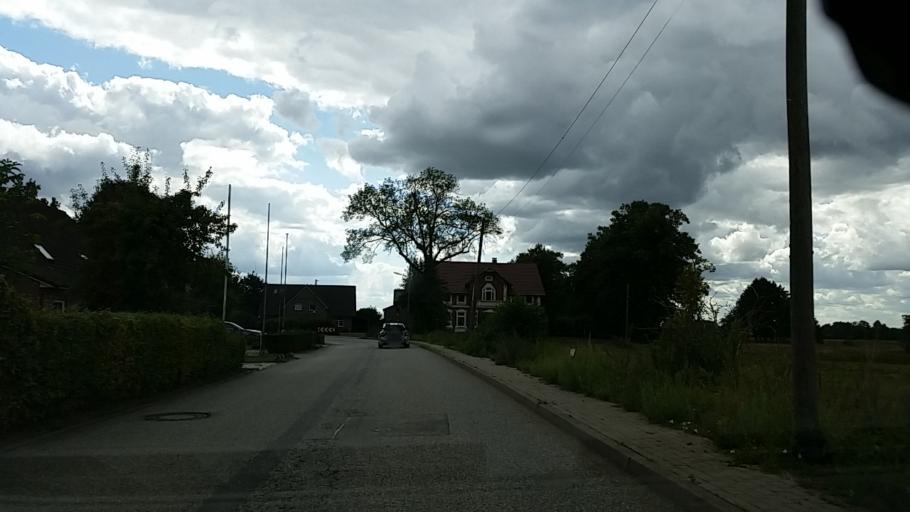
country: DE
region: Schleswig-Holstein
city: Bornsen
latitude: 53.4673
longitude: 10.2586
